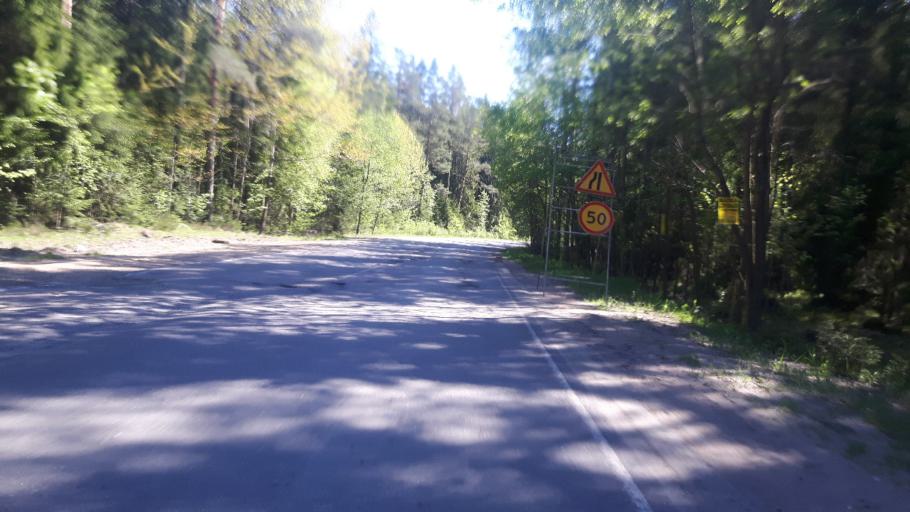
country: RU
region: Leningrad
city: Glebychevo
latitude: 60.2384
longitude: 29.0031
